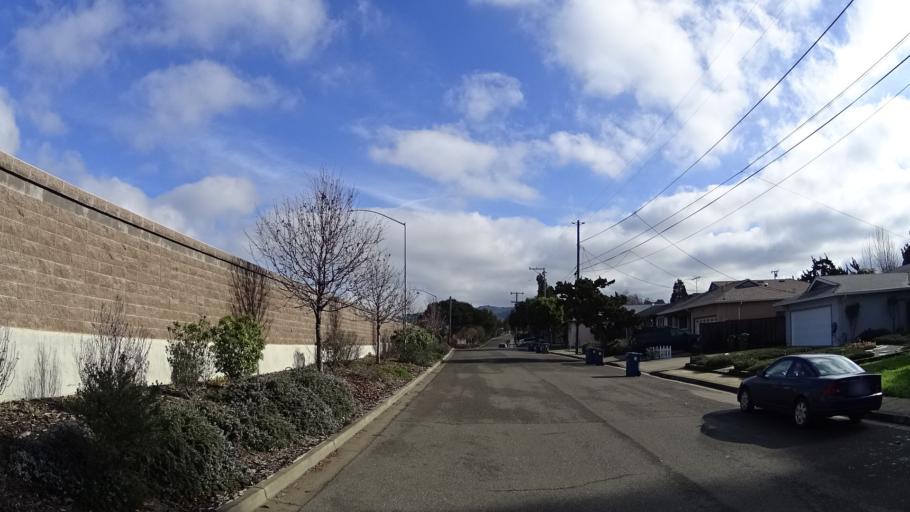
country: US
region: California
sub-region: Alameda County
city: Castro Valley
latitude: 37.6907
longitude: -122.0685
